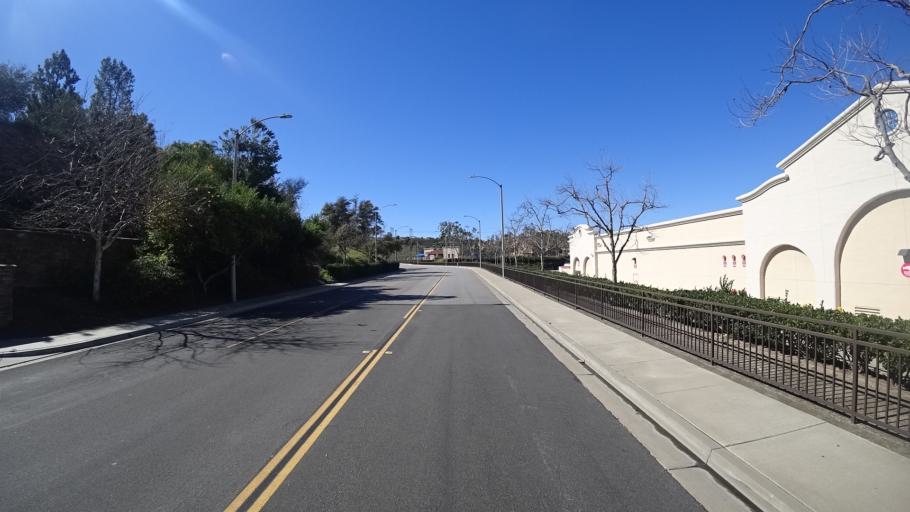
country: US
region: California
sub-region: Orange County
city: Yorba Linda
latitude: 33.8648
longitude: -117.7467
